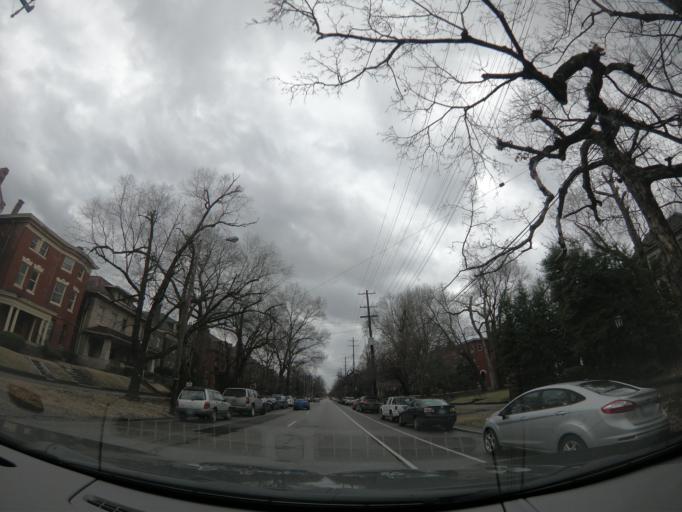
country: US
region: Kentucky
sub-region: Jefferson County
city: Louisville
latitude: 38.2309
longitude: -85.7594
